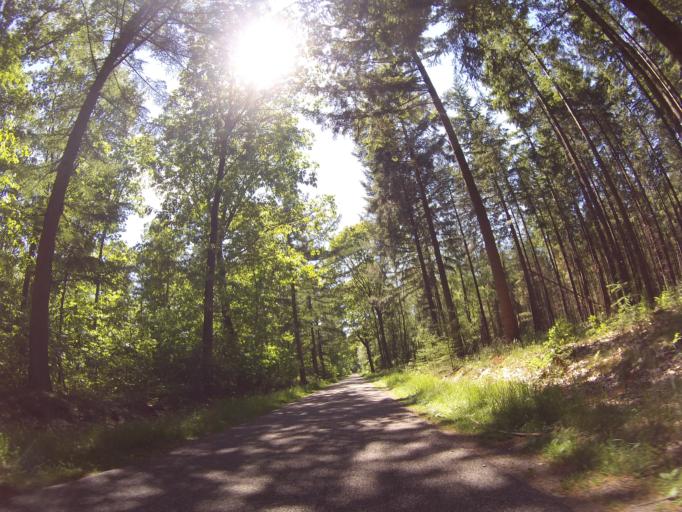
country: NL
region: Drenthe
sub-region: Gemeente Coevorden
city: Dalen
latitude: 52.7719
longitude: 6.6501
